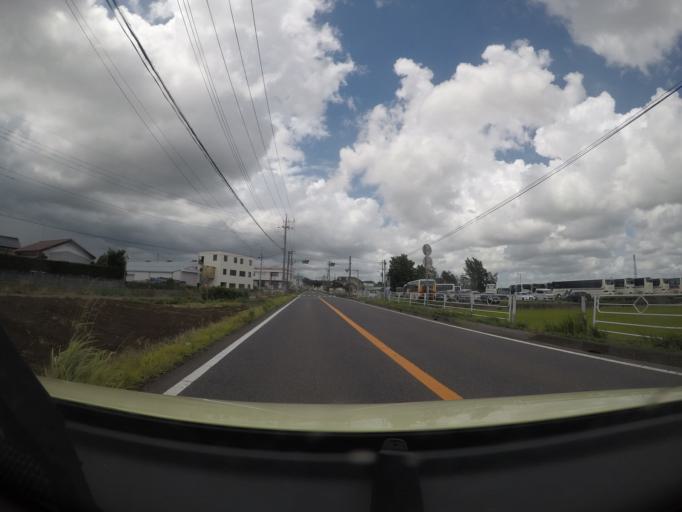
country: JP
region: Ibaraki
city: Mitsukaido
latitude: 36.0581
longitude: 139.9819
